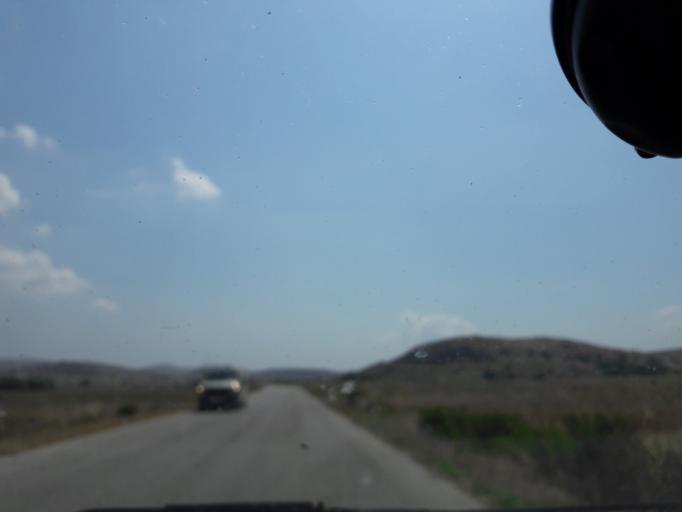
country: GR
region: North Aegean
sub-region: Nomos Lesvou
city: Myrina
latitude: 39.9154
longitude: 25.3179
